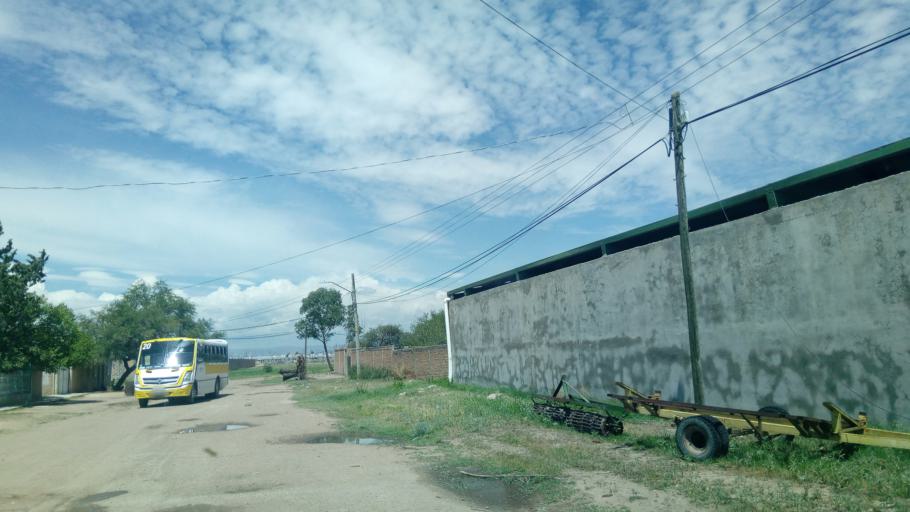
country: MX
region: Durango
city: Victoria de Durango
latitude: 24.0180
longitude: -104.5912
